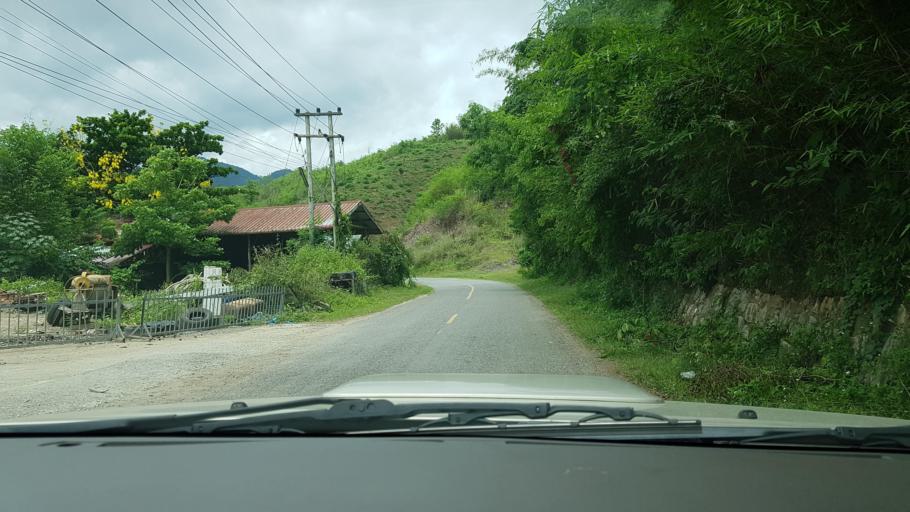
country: TH
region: Nan
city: Chaloem Phra Kiat
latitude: 19.9535
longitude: 101.2540
